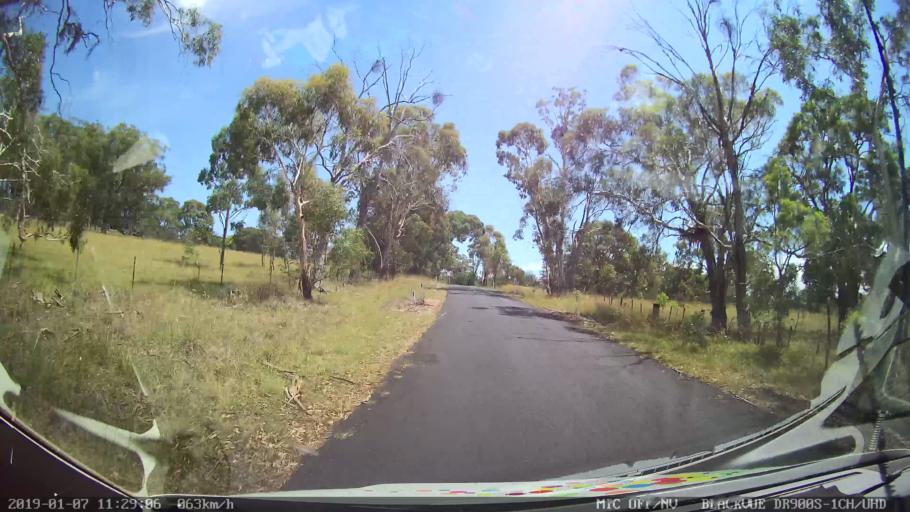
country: AU
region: New South Wales
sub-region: Armidale Dumaresq
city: Armidale
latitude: -30.4421
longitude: 151.5648
